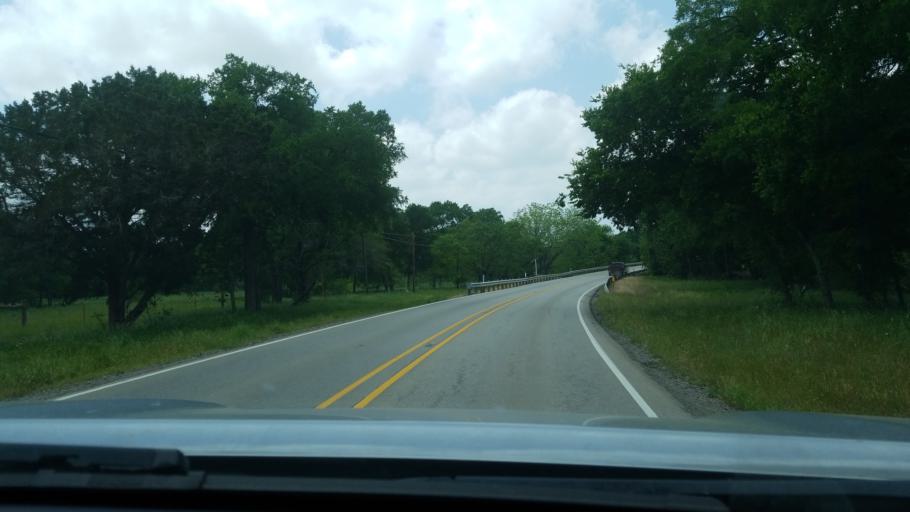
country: US
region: Texas
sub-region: Hays County
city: Dripping Springs
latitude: 30.1435
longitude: -98.0471
